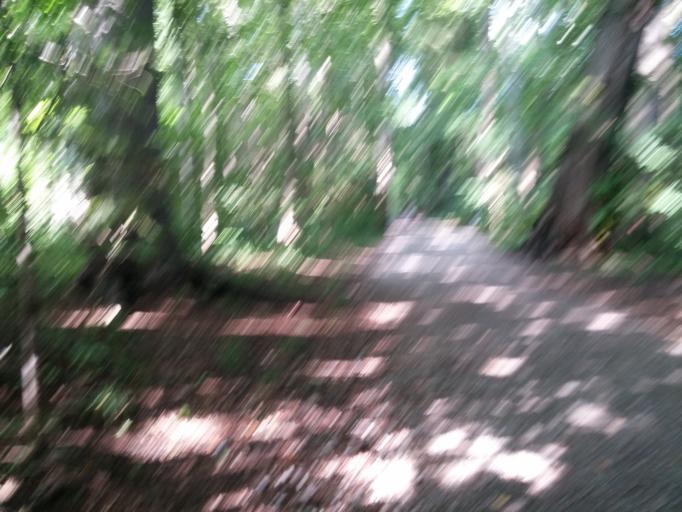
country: DE
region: Bavaria
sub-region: Upper Bavaria
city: Landsberg am Lech
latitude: 48.0423
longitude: 10.8753
